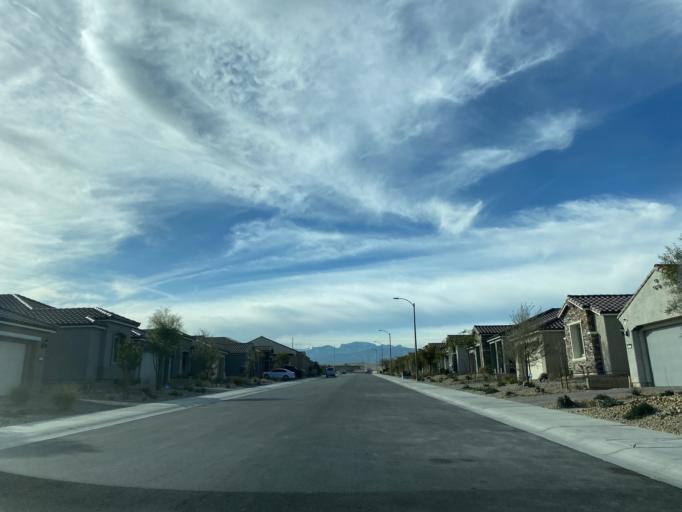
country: US
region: Nevada
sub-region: Clark County
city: Summerlin South
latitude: 36.3121
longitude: -115.3224
